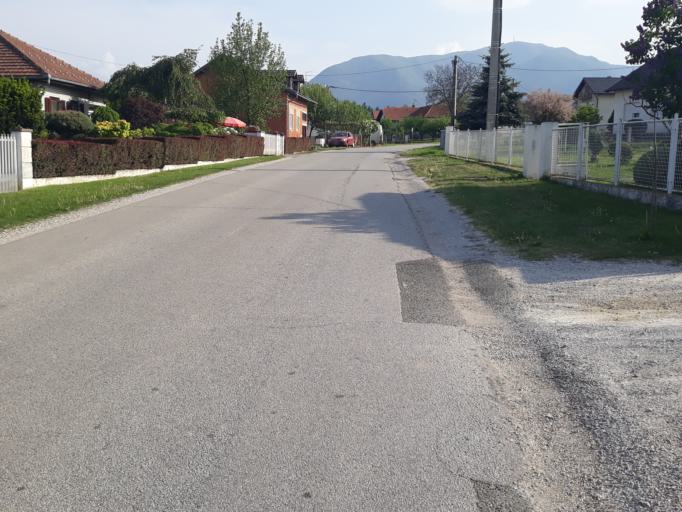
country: HR
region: Varazdinska
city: Ivanec
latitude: 46.2326
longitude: 16.1502
